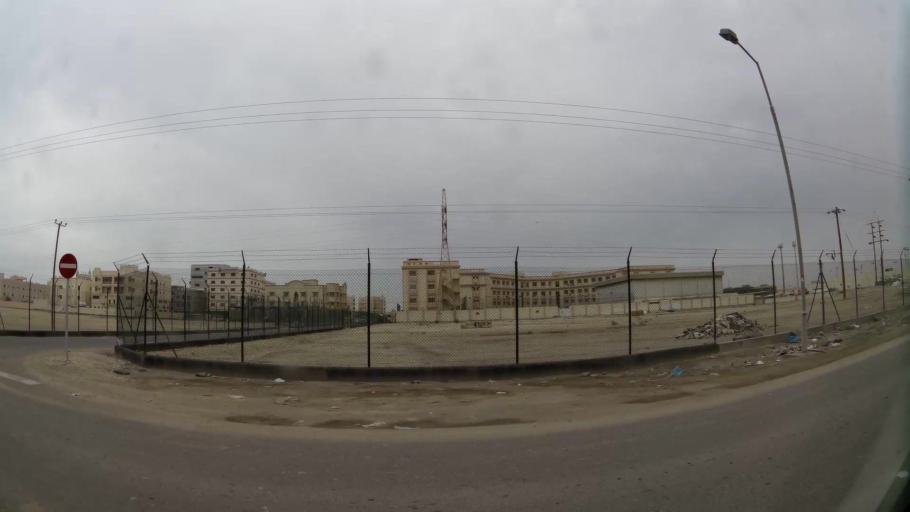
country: BH
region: Northern
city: Madinat `Isa
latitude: 26.1802
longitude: 50.5346
